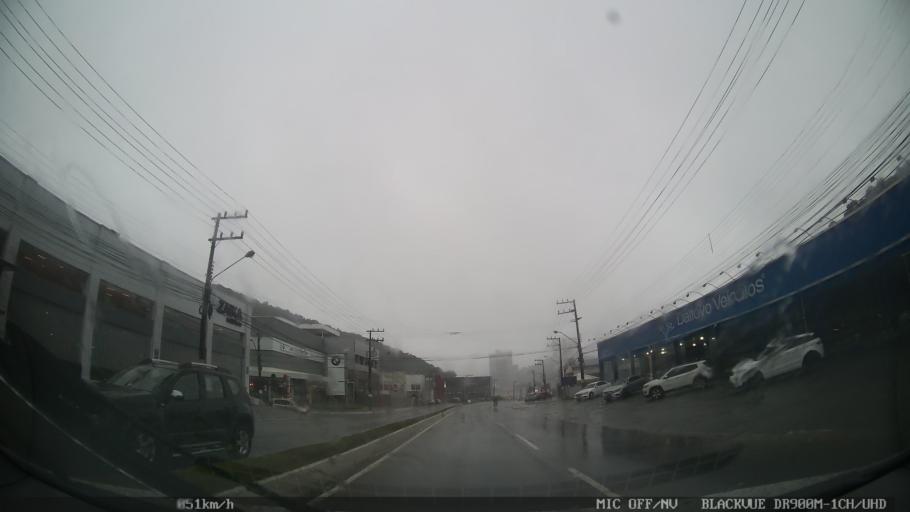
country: BR
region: Santa Catarina
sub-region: Balneario Camboriu
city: Balneario Camboriu
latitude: -26.9611
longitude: -48.6398
